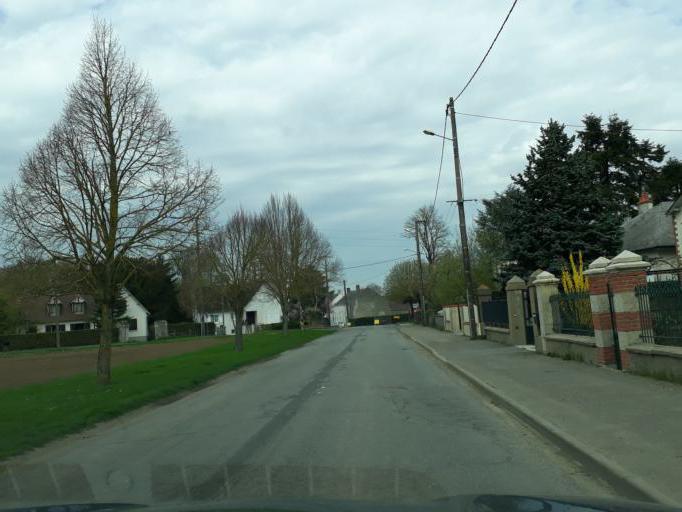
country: FR
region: Centre
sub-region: Departement du Loiret
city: Epieds-en-Beauce
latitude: 47.9456
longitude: 1.6205
